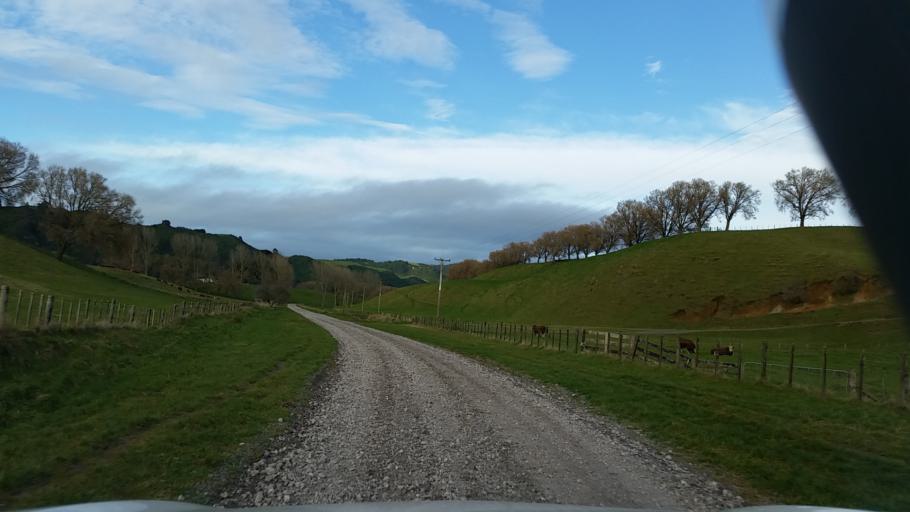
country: NZ
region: Bay of Plenty
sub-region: Rotorua District
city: Rotorua
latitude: -38.3118
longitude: 176.3026
